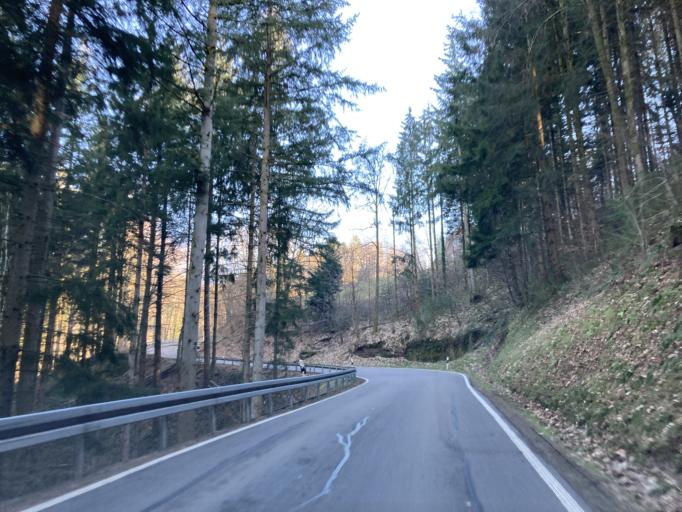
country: DE
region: Baden-Wuerttemberg
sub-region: Freiburg Region
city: Oppenau
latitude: 48.4805
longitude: 8.1948
